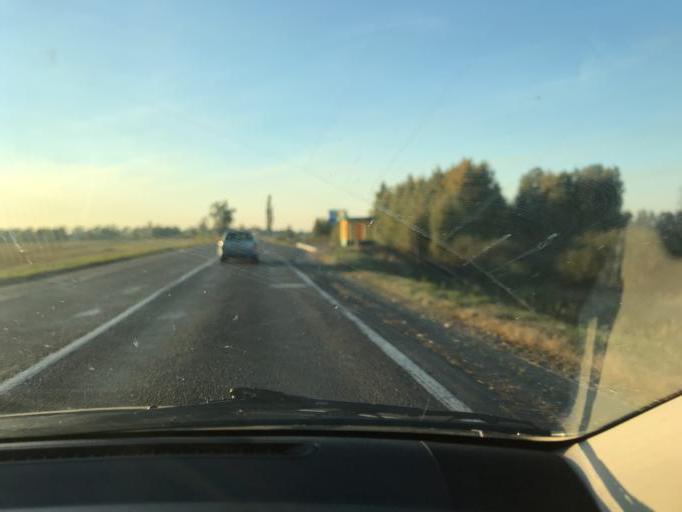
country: BY
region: Brest
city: Pinsk
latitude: 52.0703
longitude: 26.1784
